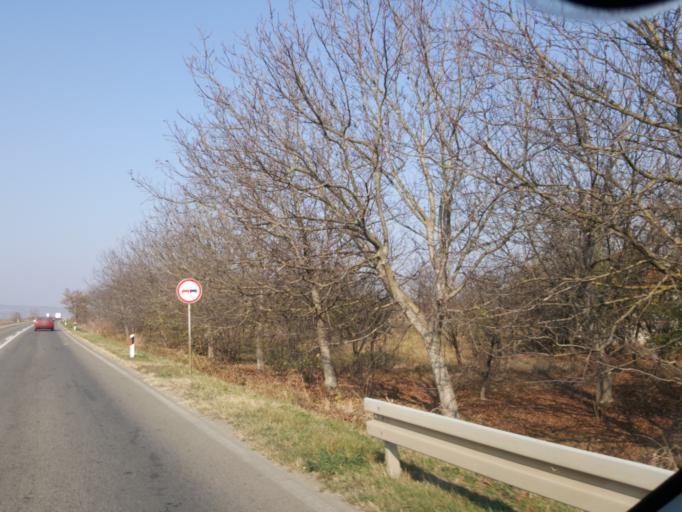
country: RS
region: Central Serbia
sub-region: Jablanicki Okrug
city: Leskovac
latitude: 43.0200
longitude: 21.9508
